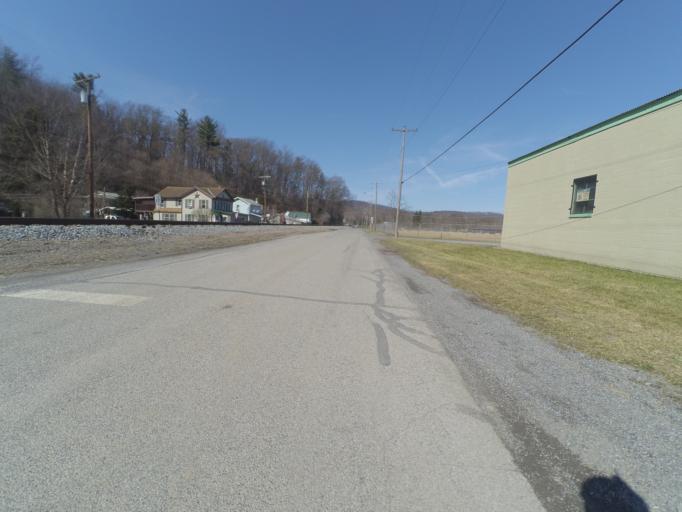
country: US
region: Pennsylvania
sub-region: Centre County
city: Milesburg
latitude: 40.9396
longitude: -77.7902
